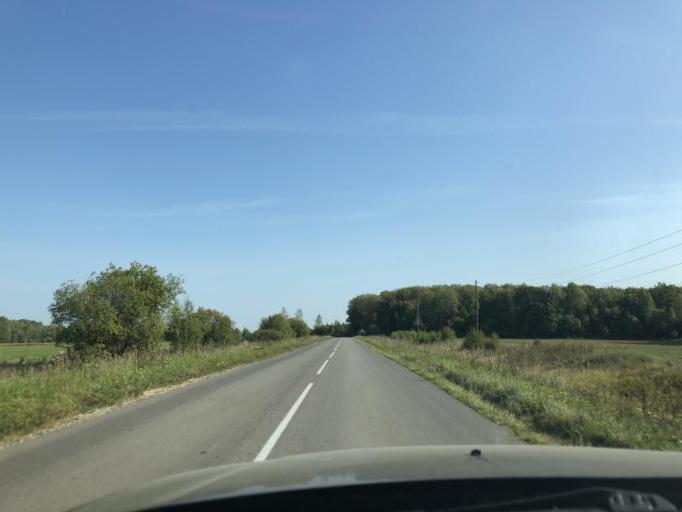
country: RU
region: Tula
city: Novogurovskiy
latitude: 54.4363
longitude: 37.3392
